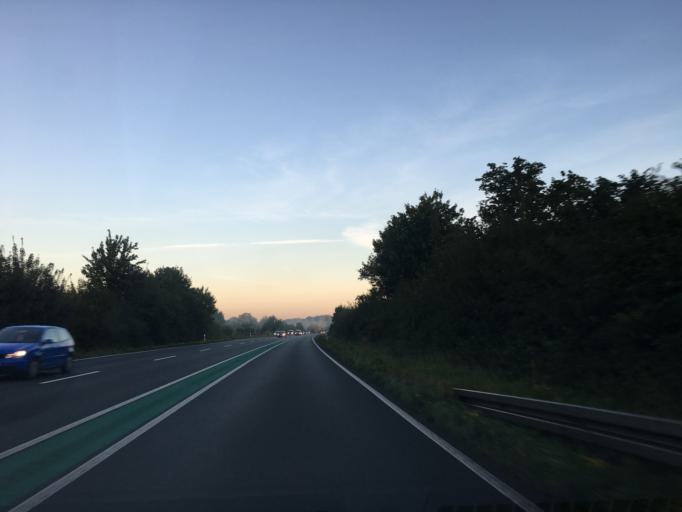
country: DE
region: North Rhine-Westphalia
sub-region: Regierungsbezirk Munster
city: Laer
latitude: 52.1080
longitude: 7.3791
